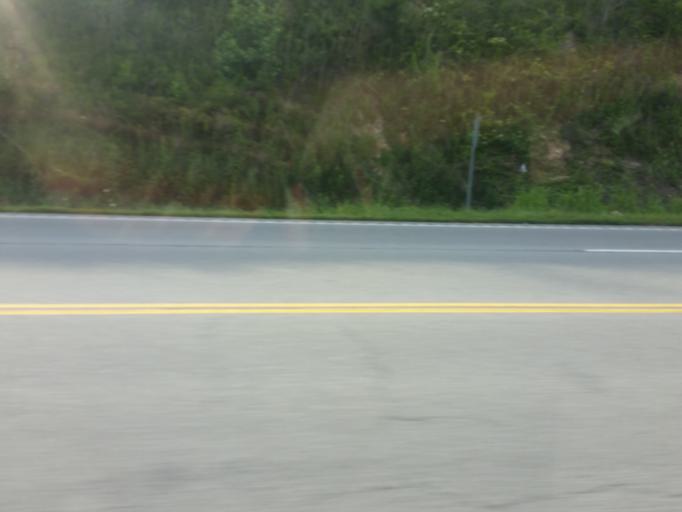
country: US
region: Tennessee
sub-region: Humphreys County
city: Johnsonville
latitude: 36.0420
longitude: -87.9271
